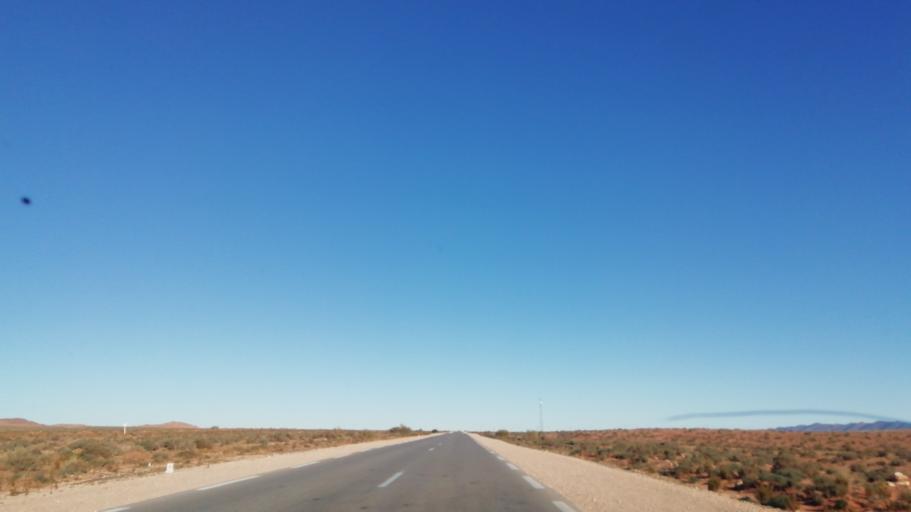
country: DZ
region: El Bayadh
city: El Abiodh Sidi Cheikh
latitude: 33.1128
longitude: 0.2317
